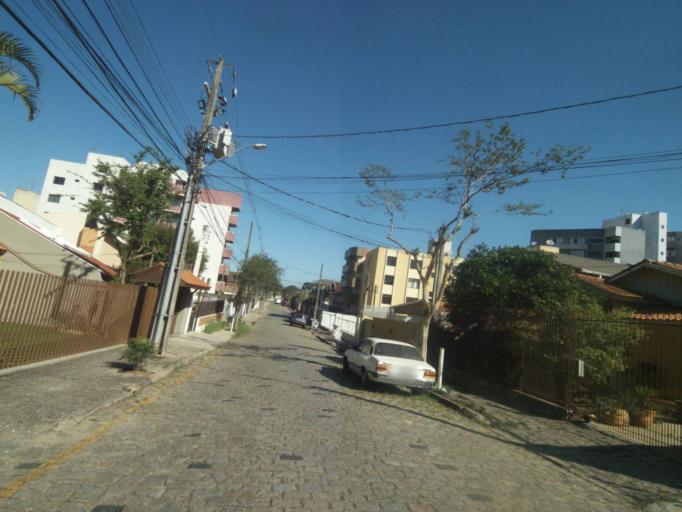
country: BR
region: Parana
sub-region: Curitiba
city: Curitiba
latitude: -25.3965
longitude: -49.2397
